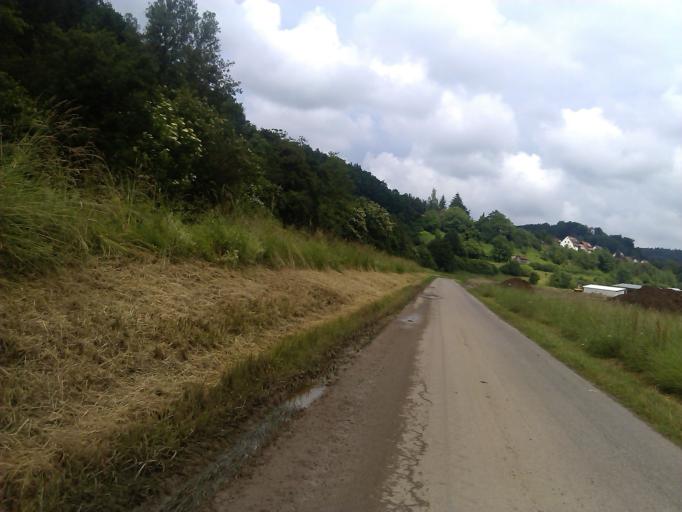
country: DE
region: Baden-Wuerttemberg
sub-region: Regierungsbezirk Stuttgart
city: Gaildorf
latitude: 48.9653
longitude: 9.8337
